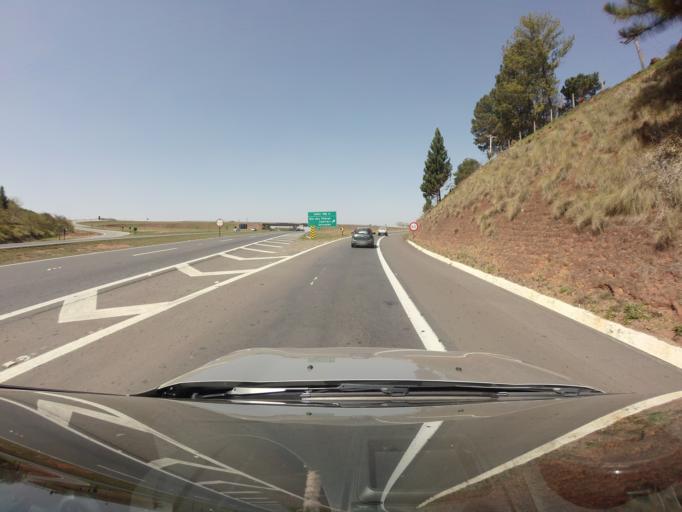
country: BR
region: Sao Paulo
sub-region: Piracicaba
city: Piracicaba
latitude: -22.7215
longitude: -47.6095
